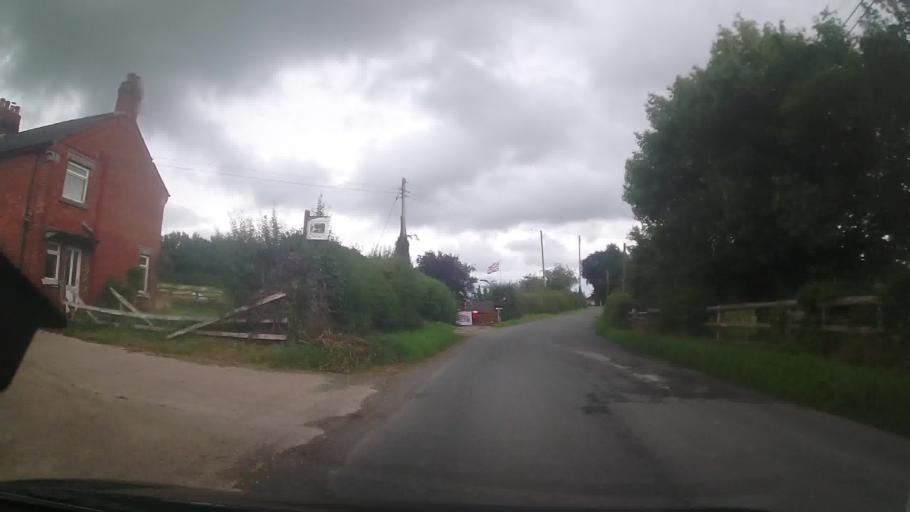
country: GB
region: England
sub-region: Shropshire
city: Whitchurch
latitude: 52.9480
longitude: -2.7322
